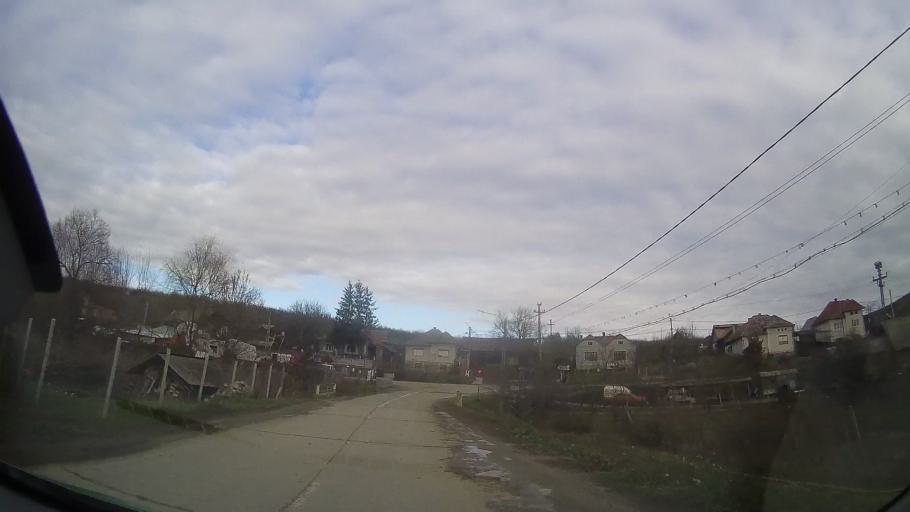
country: RO
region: Bistrita-Nasaud
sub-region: Comuna Sanmihaiu de Campie
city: Sanmihaiu de Campie
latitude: 46.8968
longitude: 24.3368
